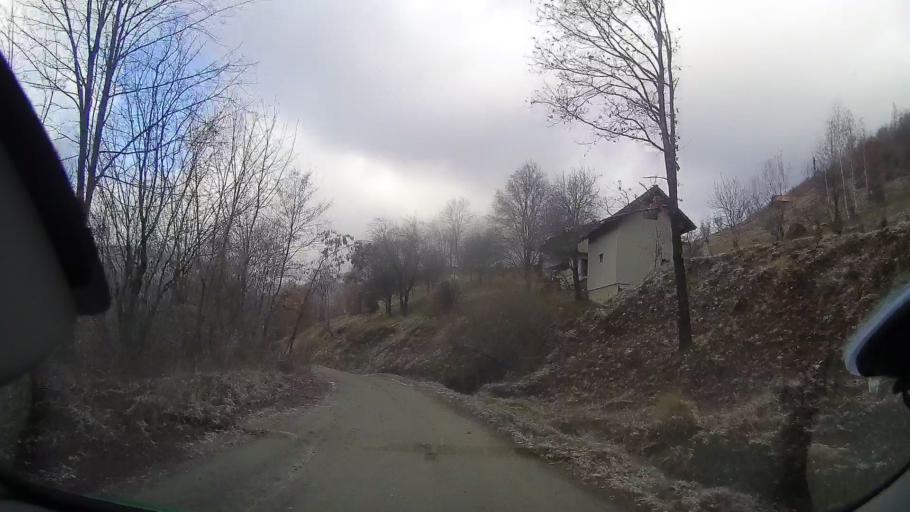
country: RO
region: Cluj
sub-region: Comuna Valea Ierii
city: Valea Ierii
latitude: 46.6763
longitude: 23.3156
